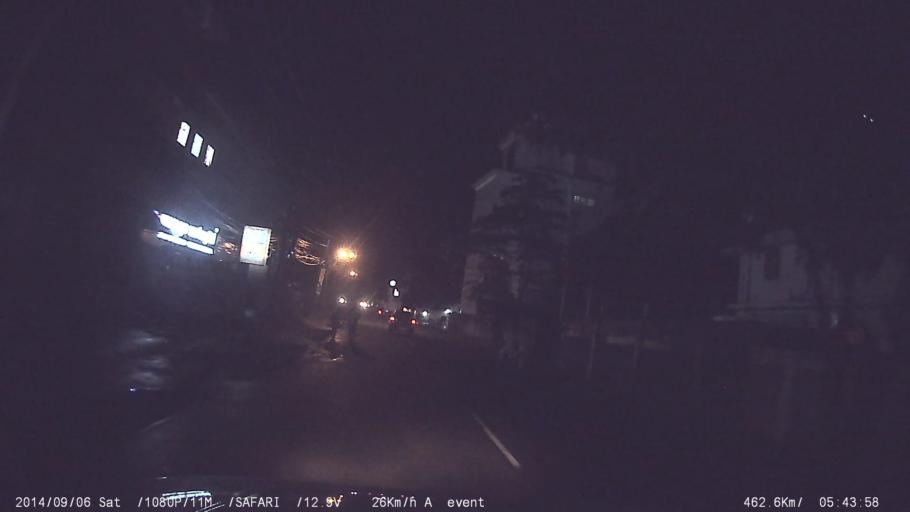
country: IN
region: Kerala
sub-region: Ernakulam
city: Cochin
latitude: 9.9655
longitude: 76.3190
